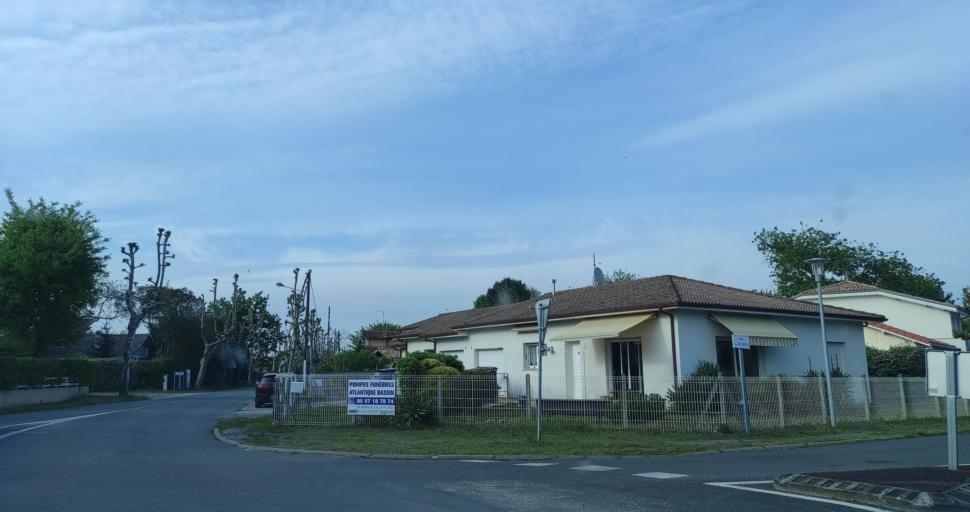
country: FR
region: Aquitaine
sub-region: Departement de la Gironde
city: Ares
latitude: 44.7607
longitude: -1.1326
